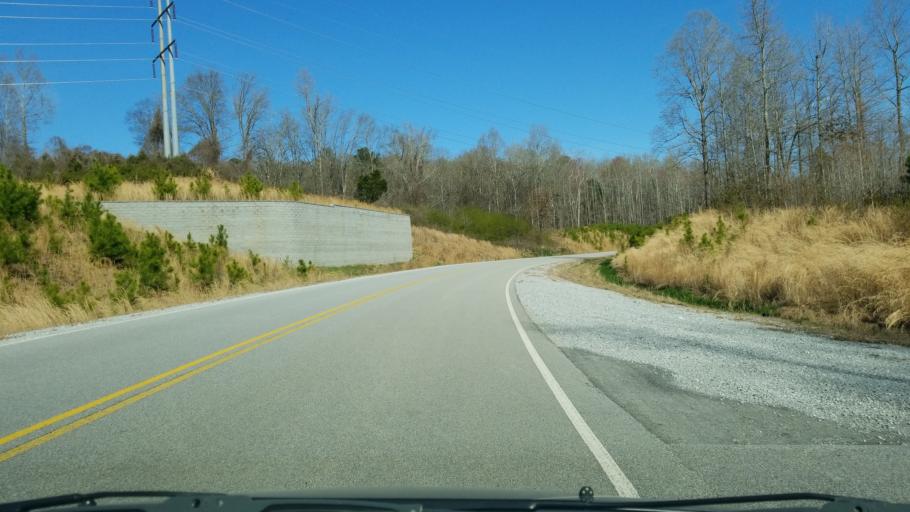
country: US
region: Tennessee
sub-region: Hamilton County
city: Harrison
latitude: 35.0956
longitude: -85.1361
